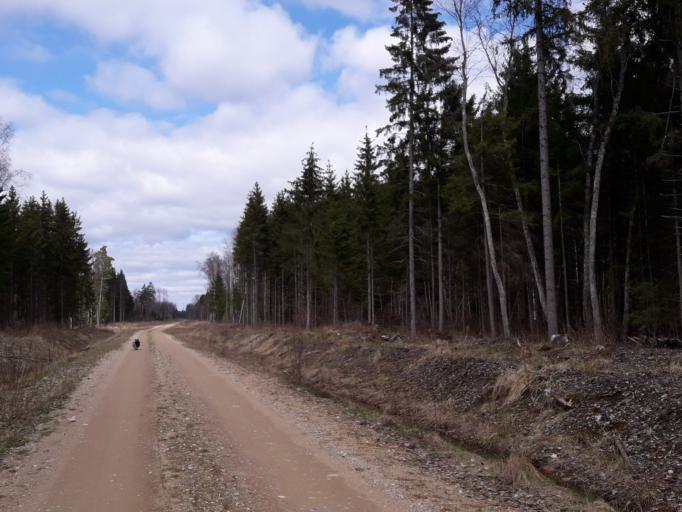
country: LV
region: Talsu Rajons
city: Sabile
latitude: 56.8925
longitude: 22.3805
